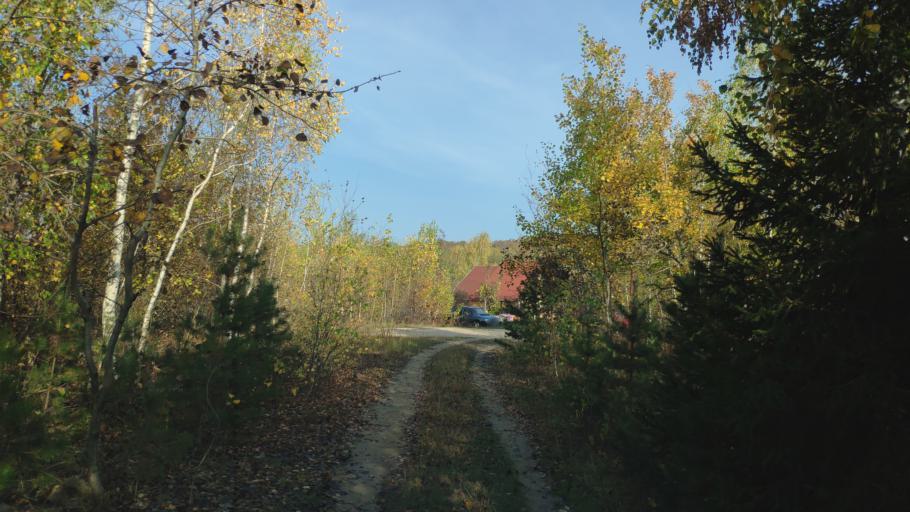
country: SK
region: Kosicky
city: Kosice
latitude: 48.7402
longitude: 21.2185
